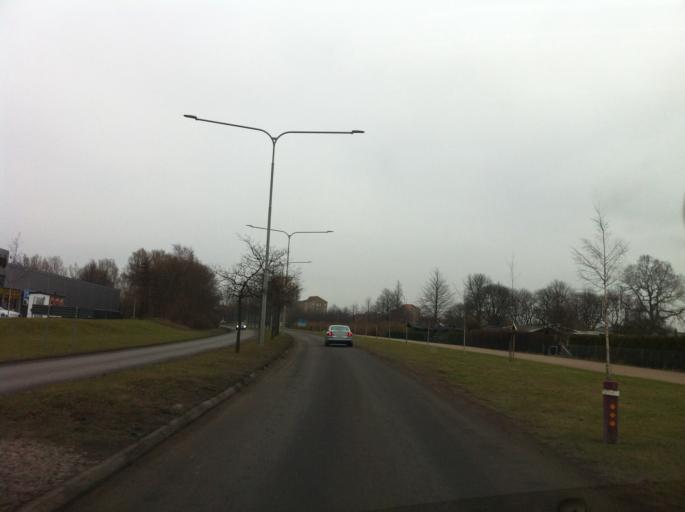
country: SE
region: Skane
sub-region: Landskrona
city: Landskrona
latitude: 55.8866
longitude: 12.8262
